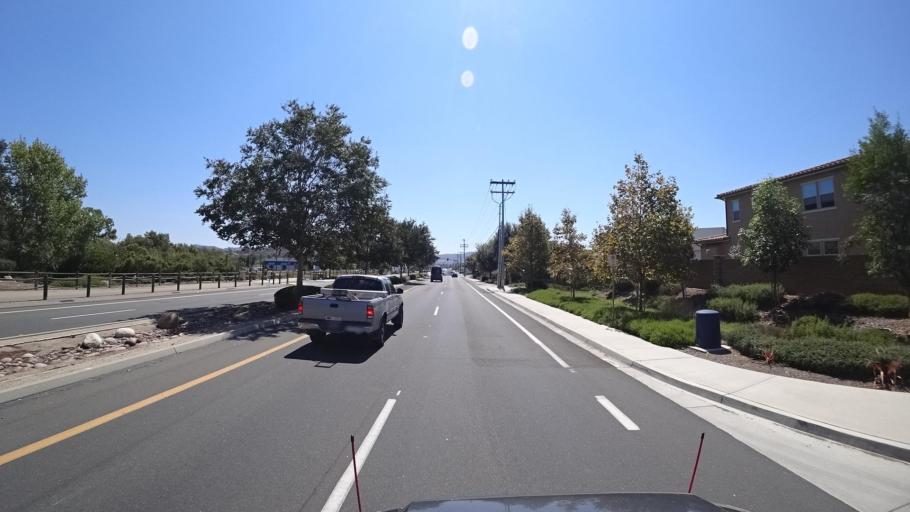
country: US
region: California
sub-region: San Diego County
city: San Marcos
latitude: 33.1541
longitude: -117.1615
